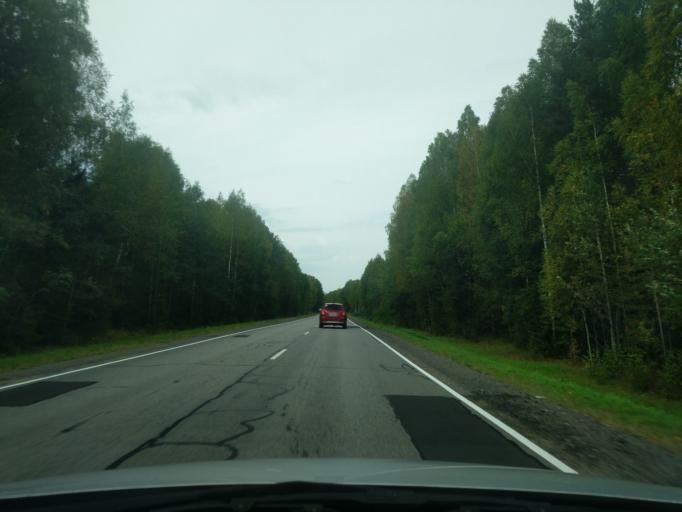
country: RU
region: Kirov
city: Kotel'nich
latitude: 58.2712
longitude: 48.0846
